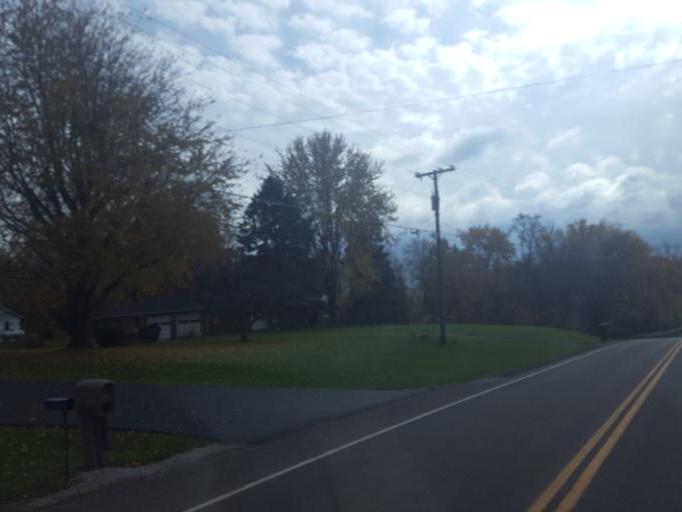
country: US
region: Ohio
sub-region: Crawford County
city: Galion
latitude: 40.7794
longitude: -82.7905
